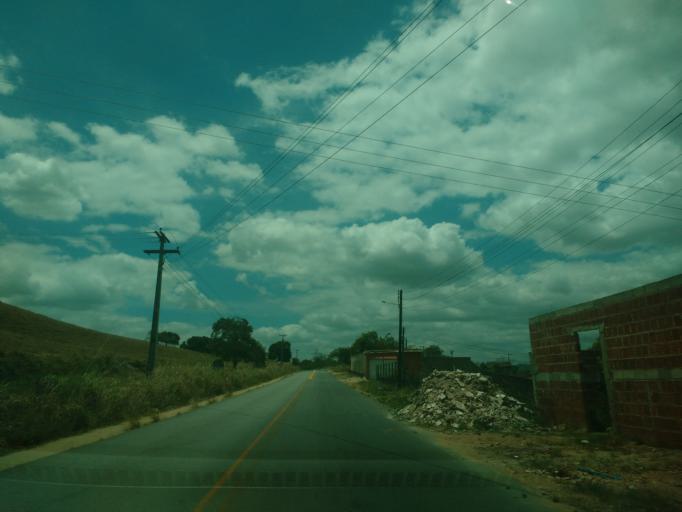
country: BR
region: Alagoas
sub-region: Uniao Dos Palmares
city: Uniao dos Palmares
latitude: -9.1417
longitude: -36.0399
